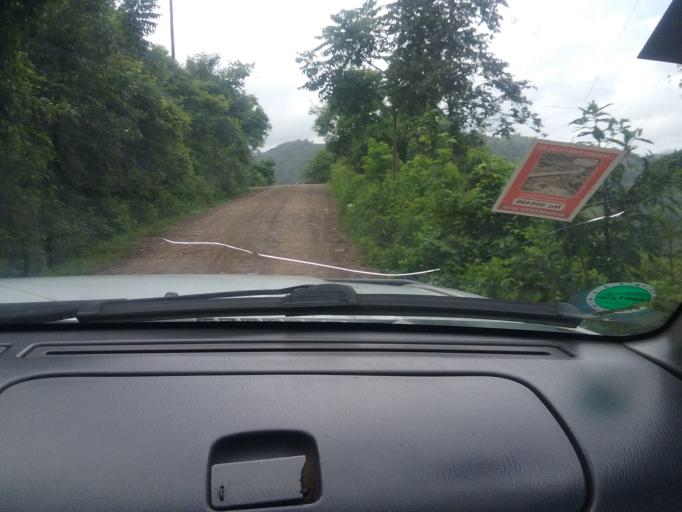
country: NI
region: Matagalpa
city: Matagalpa
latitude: 12.8726
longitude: -85.9558
